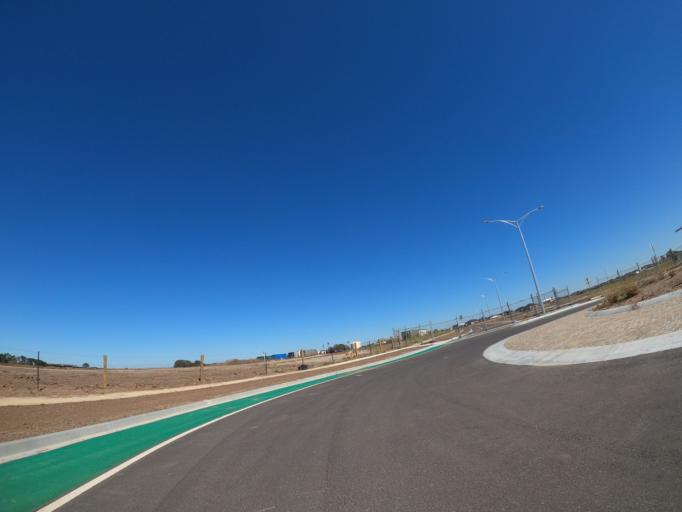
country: AU
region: Victoria
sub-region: Hume
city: Craigieburn
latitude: -37.5317
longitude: 144.9137
